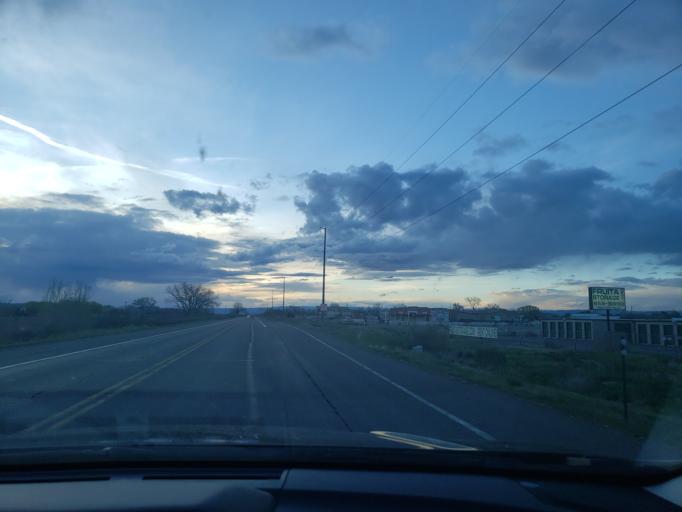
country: US
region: Colorado
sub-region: Mesa County
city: Fruita
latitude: 39.1322
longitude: -108.6878
